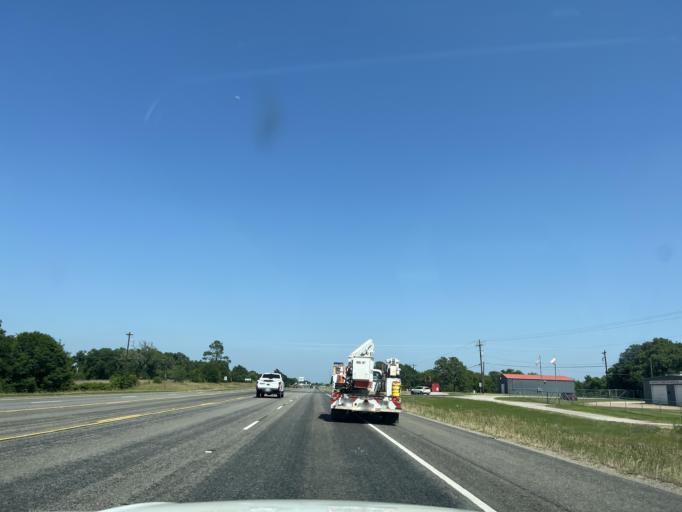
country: US
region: Texas
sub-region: Washington County
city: Brenham
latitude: 30.1718
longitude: -96.4480
